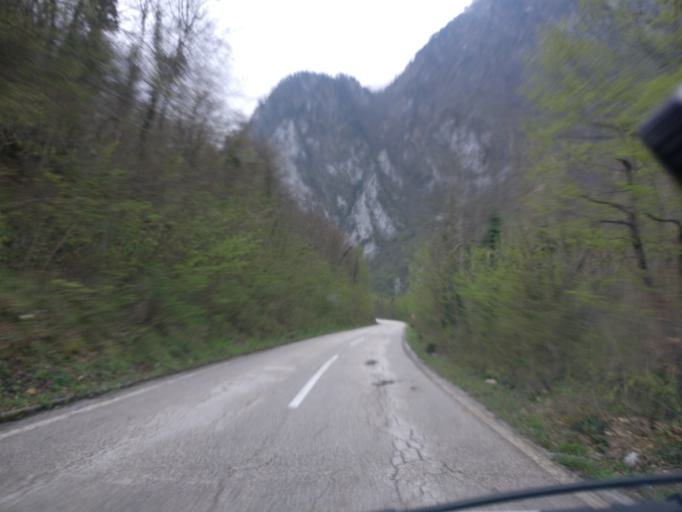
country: ME
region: Opstina Pluzine
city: Pluzine
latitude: 43.3064
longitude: 18.8512
